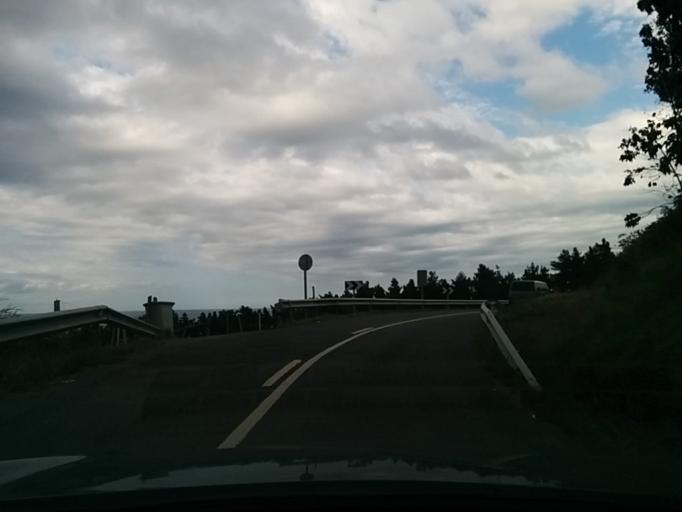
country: ES
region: Basque Country
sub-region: Bizkaia
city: Lekeitio
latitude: 43.3623
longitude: -2.4909
